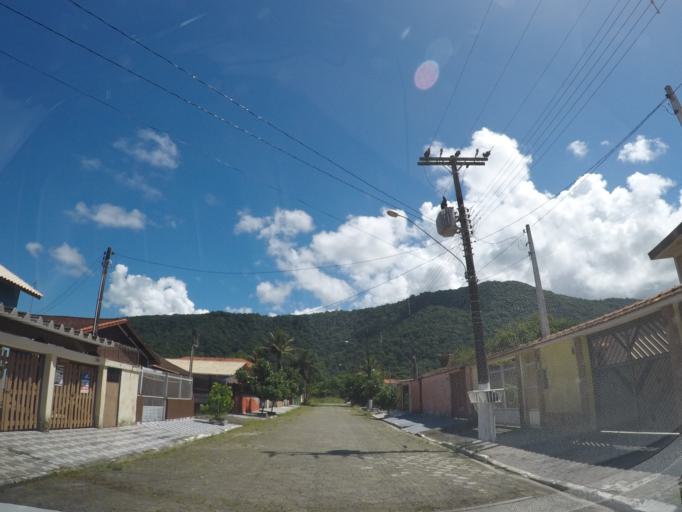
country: BR
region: Sao Paulo
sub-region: Mongagua
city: Mongagua
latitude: -24.0800
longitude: -46.5928
